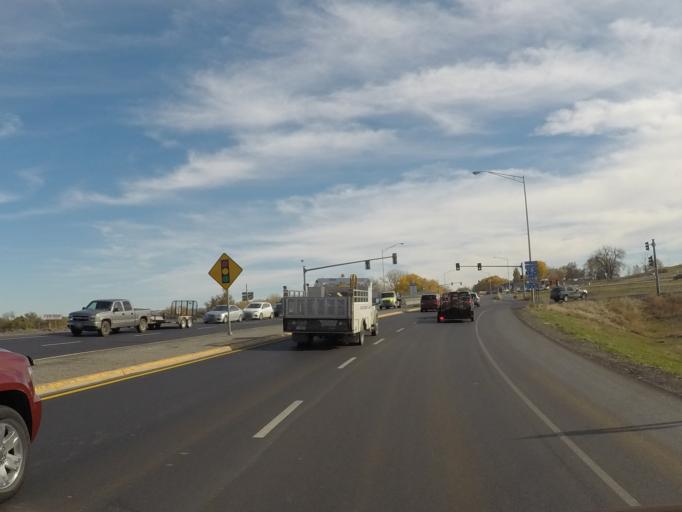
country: US
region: Montana
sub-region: Yellowstone County
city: Billings
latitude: 45.7971
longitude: -108.4590
